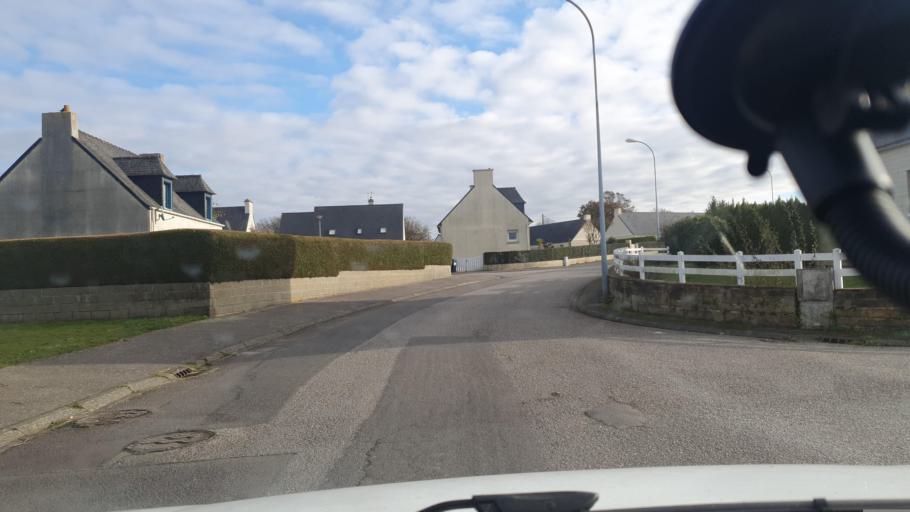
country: FR
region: Brittany
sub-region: Departement du Finistere
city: Briec
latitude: 48.1040
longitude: -4.0070
